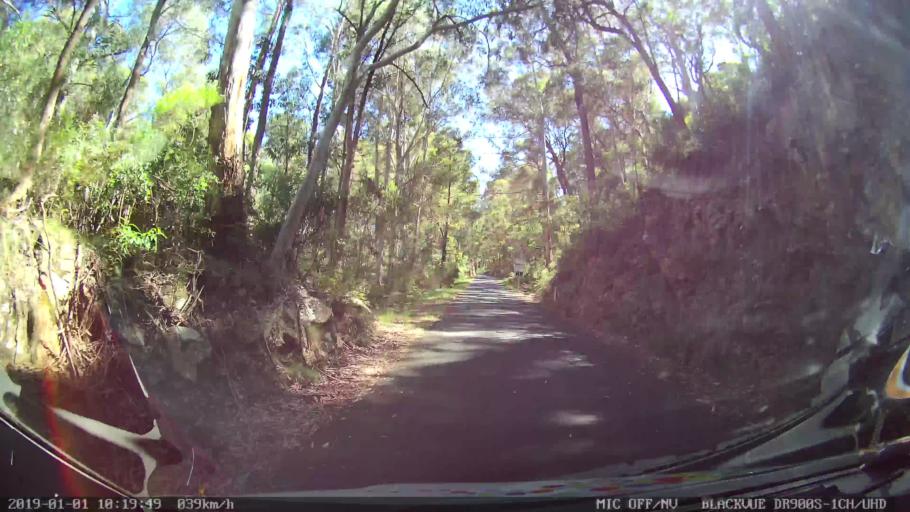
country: AU
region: New South Wales
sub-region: Snowy River
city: Jindabyne
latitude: -36.0821
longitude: 148.1863
